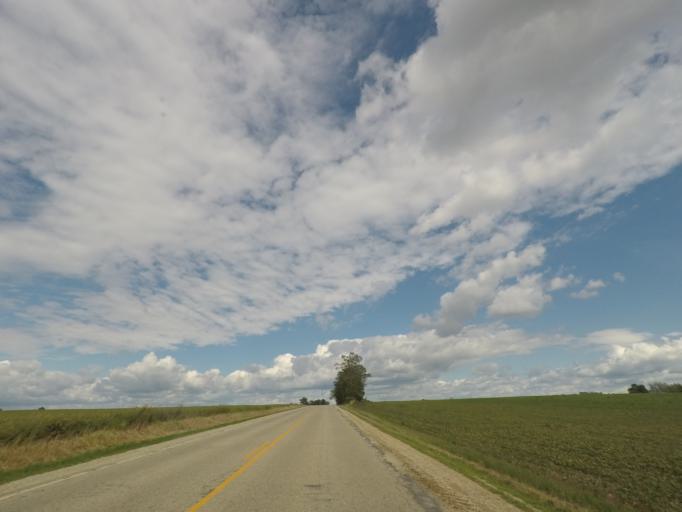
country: US
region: Wisconsin
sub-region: Rock County
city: Orfordville
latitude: 42.7053
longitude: -89.1623
